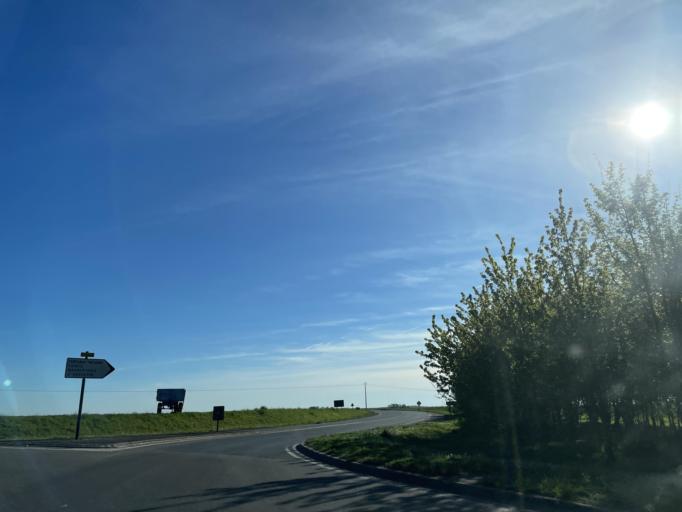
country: FR
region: Ile-de-France
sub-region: Departement de Seine-et-Marne
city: Coulommiers
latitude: 48.7968
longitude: 3.0737
